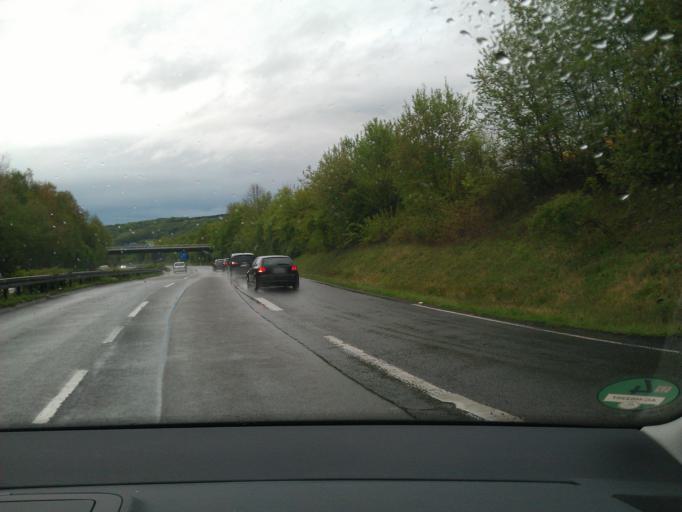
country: DE
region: North Rhine-Westphalia
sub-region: Regierungsbezirk Koln
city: Hennef
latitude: 50.7678
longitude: 7.3112
